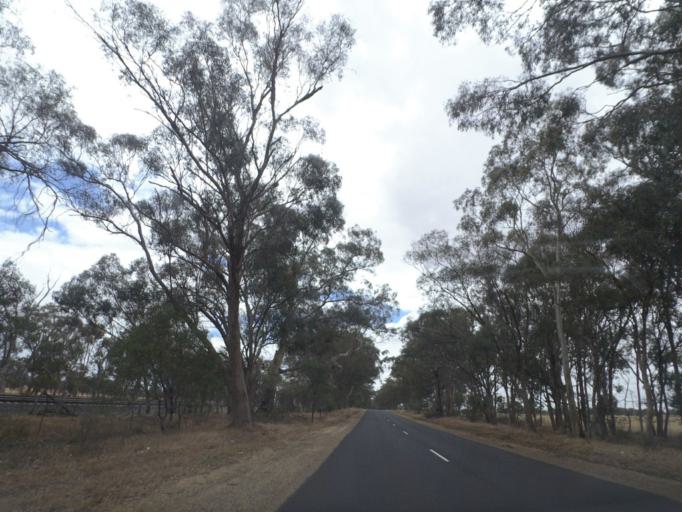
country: AU
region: Victoria
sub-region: Murrindindi
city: Kinglake West
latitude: -36.9637
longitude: 145.1672
